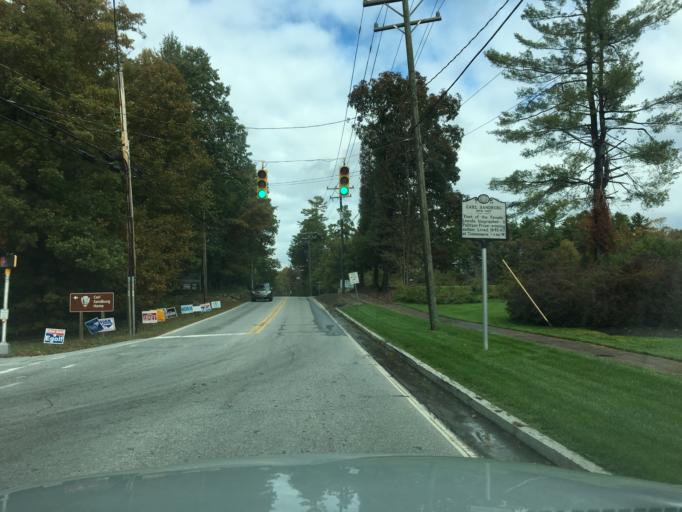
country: US
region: North Carolina
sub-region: Henderson County
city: Flat Rock
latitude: 35.2727
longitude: -82.4419
